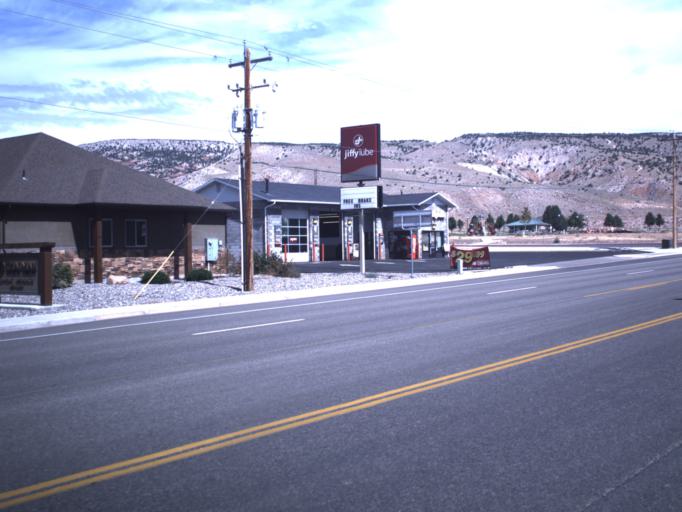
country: US
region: Utah
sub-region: Sevier County
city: Richfield
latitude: 38.7812
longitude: -112.0847
